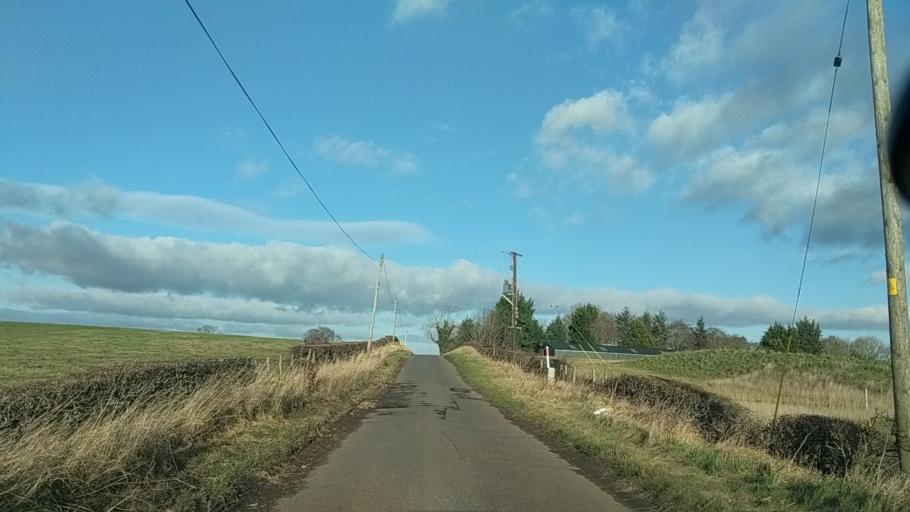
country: GB
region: Scotland
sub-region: Edinburgh
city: Kirkliston
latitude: 55.9738
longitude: -3.4368
